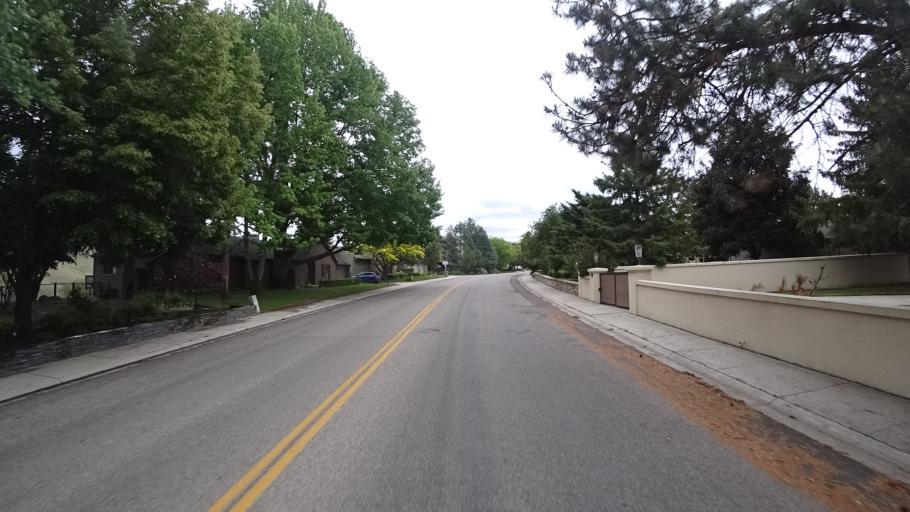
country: US
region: Idaho
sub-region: Ada County
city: Boise
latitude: 43.6155
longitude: -116.1629
